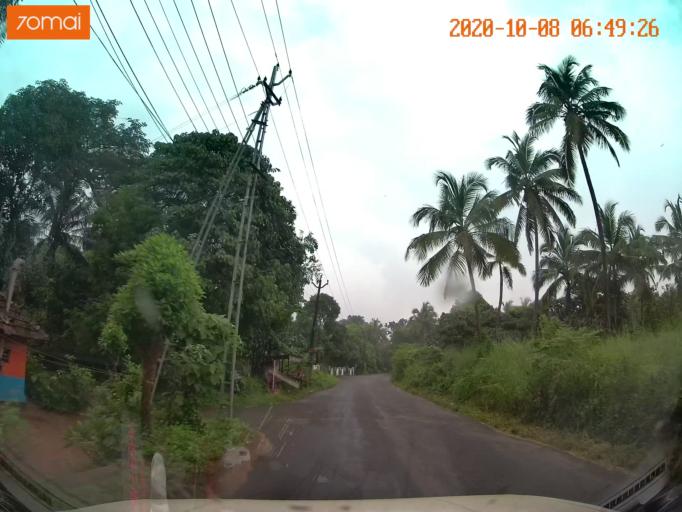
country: IN
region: Kerala
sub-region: Thrissur District
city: Kunnamkulam
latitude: 10.6833
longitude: 76.1027
